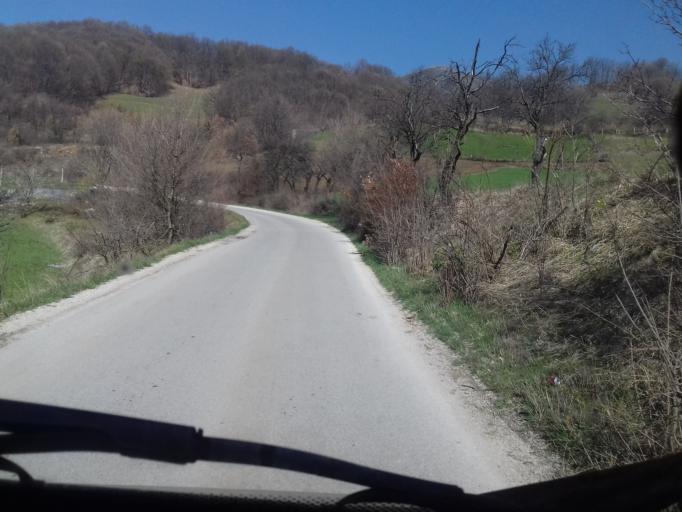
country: BA
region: Federation of Bosnia and Herzegovina
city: Travnik
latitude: 44.2370
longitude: 17.7181
